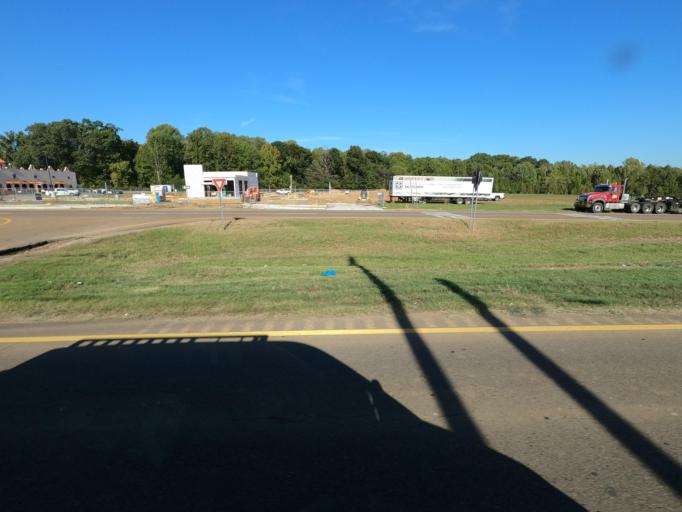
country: US
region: Tennessee
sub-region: Tipton County
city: Atoka
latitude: 35.4459
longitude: -89.7866
